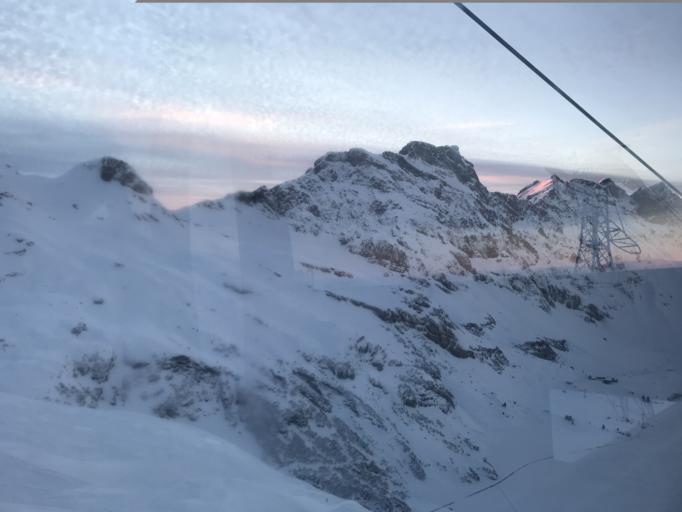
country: CH
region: Obwalden
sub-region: Obwalden
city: Engelberg
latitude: 46.7868
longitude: 8.4093
